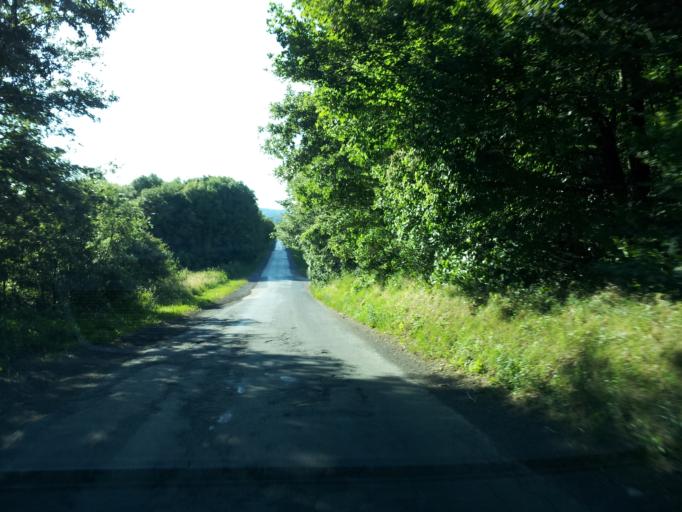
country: HU
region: Veszprem
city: Zirc
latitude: 47.2191
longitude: 17.8383
